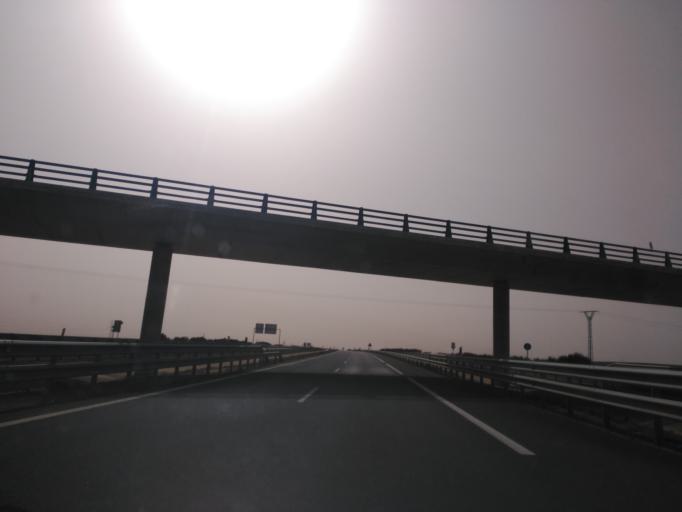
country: ES
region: Castille and Leon
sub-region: Provincia de Palencia
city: Abia de las Torres
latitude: 42.4025
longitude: -4.3885
